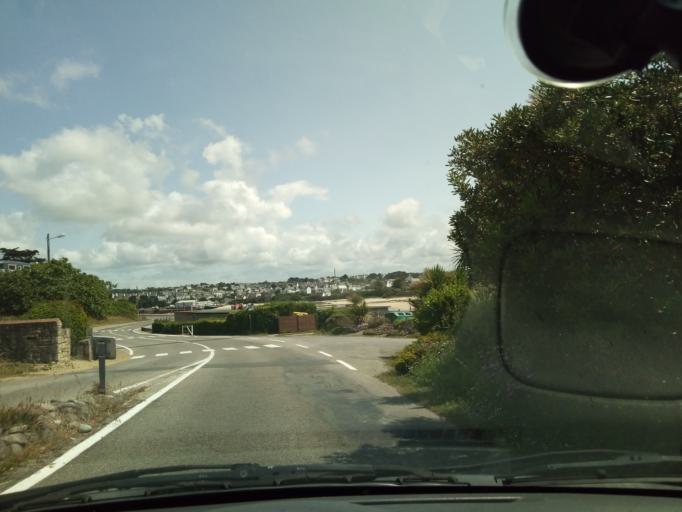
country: FR
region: Brittany
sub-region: Departement du Finistere
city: Audierne
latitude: 48.0127
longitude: -4.5416
